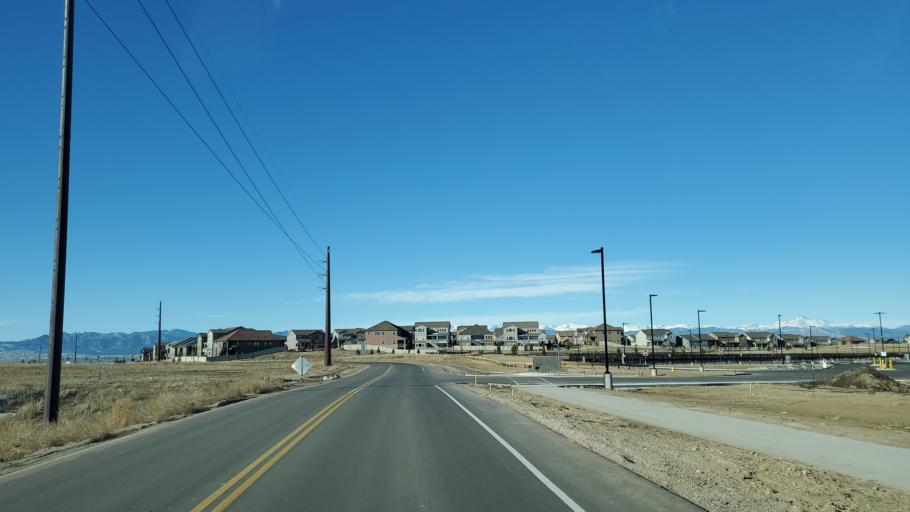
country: US
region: Colorado
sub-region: Boulder County
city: Lafayette
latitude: 39.9867
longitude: -105.0213
